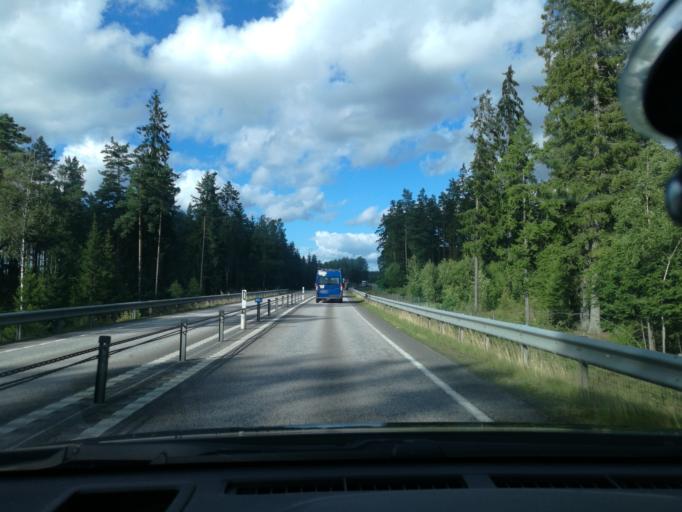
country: SE
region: Kronoberg
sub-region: Vaxjo Kommun
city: Braas
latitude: 57.0283
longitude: 15.0622
